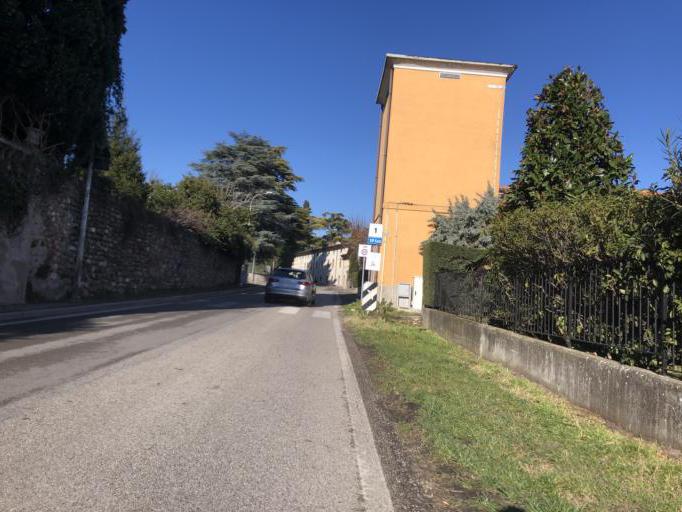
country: IT
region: Veneto
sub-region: Provincia di Verona
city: Sona
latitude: 45.4315
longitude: 10.8363
